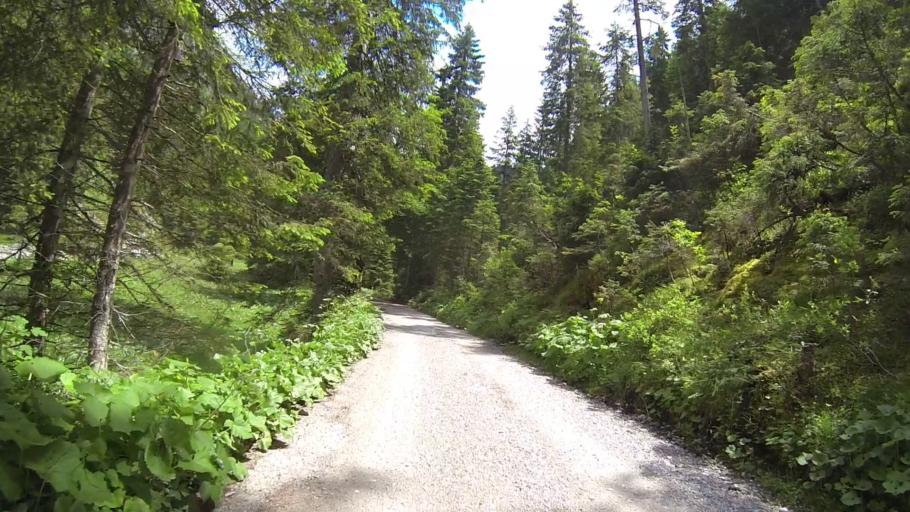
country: DE
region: Bavaria
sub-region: Swabia
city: Schwangau
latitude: 47.5340
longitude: 10.7883
